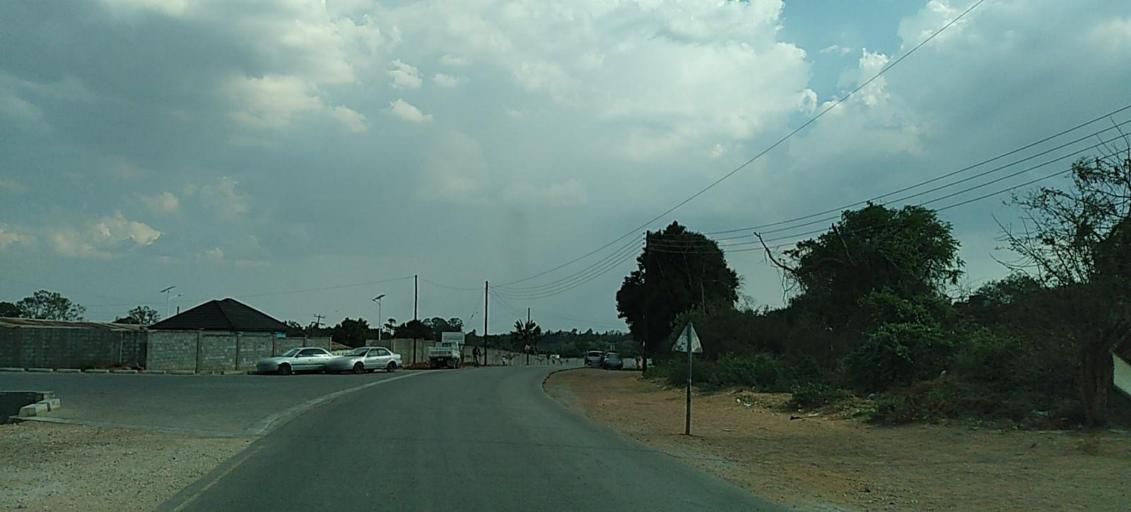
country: ZM
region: Lusaka
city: Lusaka
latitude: -15.5144
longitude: 28.2373
